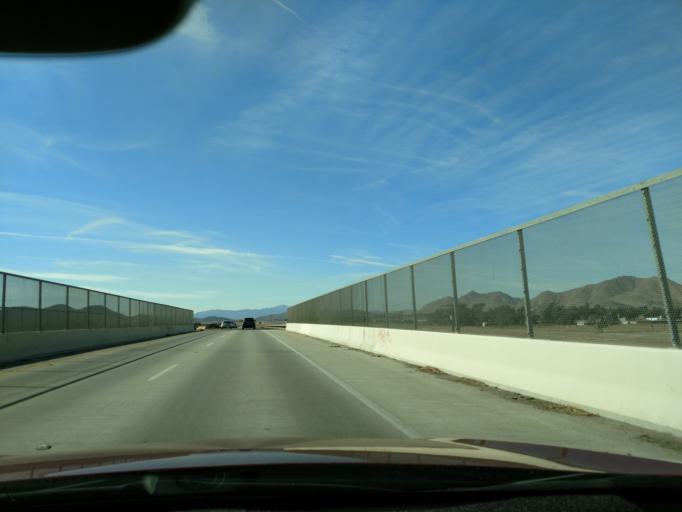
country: US
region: California
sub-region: Riverside County
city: Winchester
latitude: 33.6986
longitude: -117.0472
